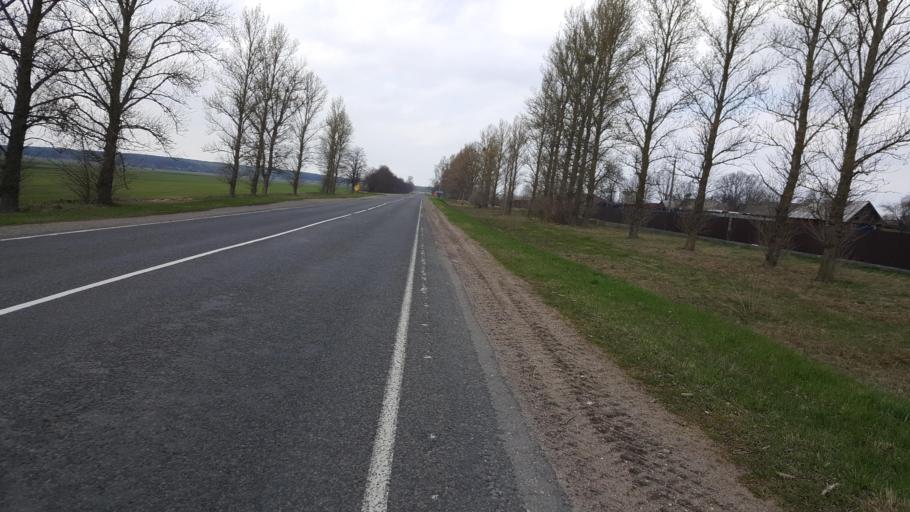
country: BY
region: Brest
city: Kamyanyets
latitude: 52.3551
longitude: 23.8962
